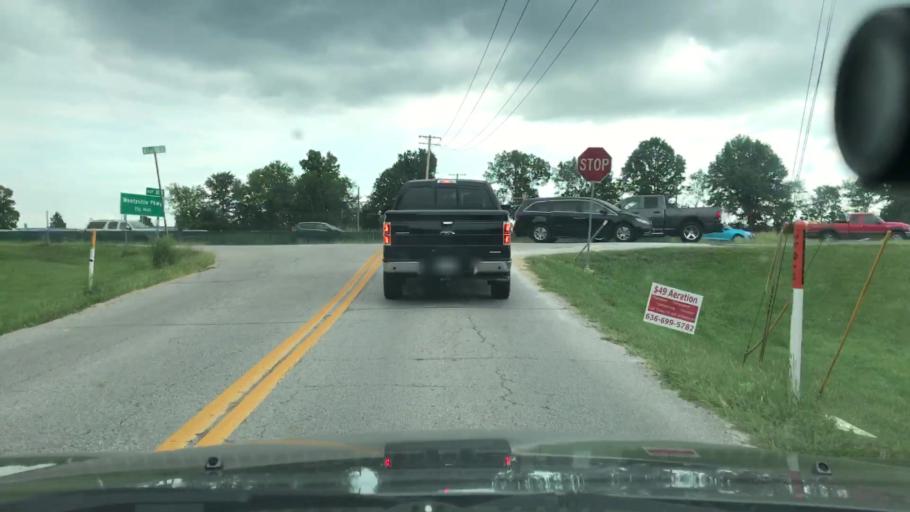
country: US
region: Missouri
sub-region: Saint Charles County
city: Wentzville
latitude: 38.8056
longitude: -90.9060
